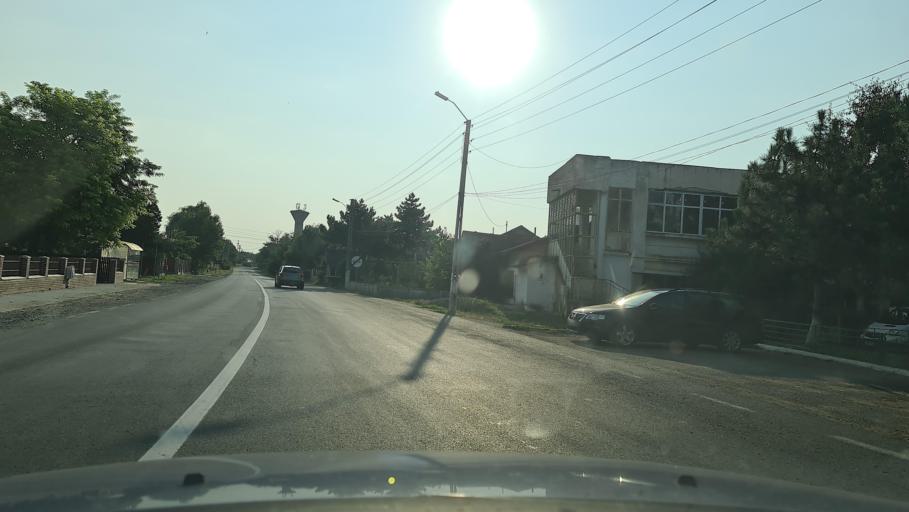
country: RO
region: Calarasi
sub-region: Comuna Dor Marunt
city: Dor Marunt
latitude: 44.4358
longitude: 26.9532
